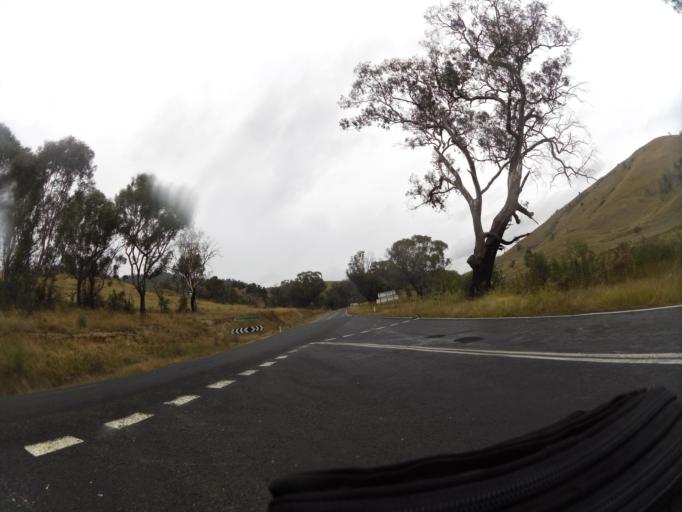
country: AU
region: New South Wales
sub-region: Greater Hume Shire
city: Holbrook
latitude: -36.2214
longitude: 147.7295
